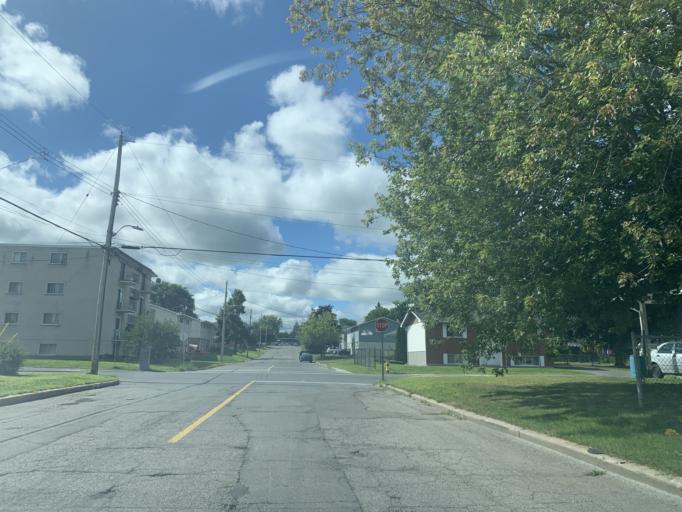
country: CA
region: Ontario
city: Hawkesbury
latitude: 45.6054
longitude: -74.5852
